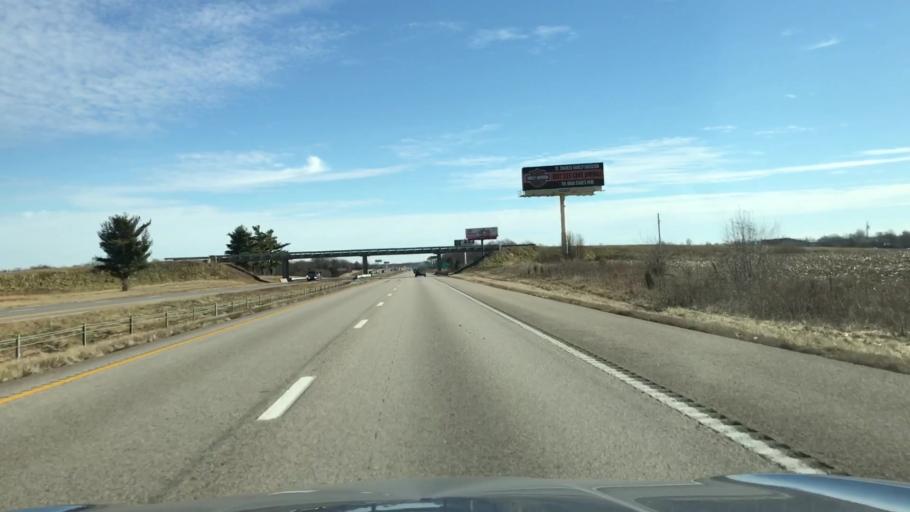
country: US
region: Missouri
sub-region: Gasconade County
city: Hermann
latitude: 38.8679
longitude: -91.3322
